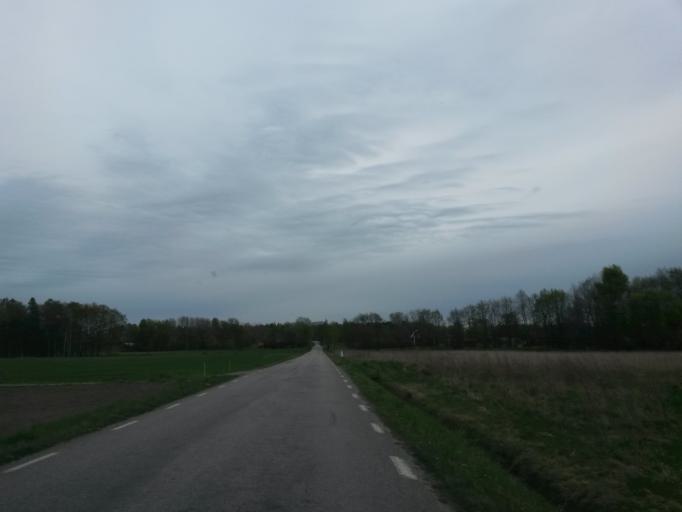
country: SE
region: Vaestra Goetaland
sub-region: Vara Kommun
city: Vara
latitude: 58.3658
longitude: 12.8598
